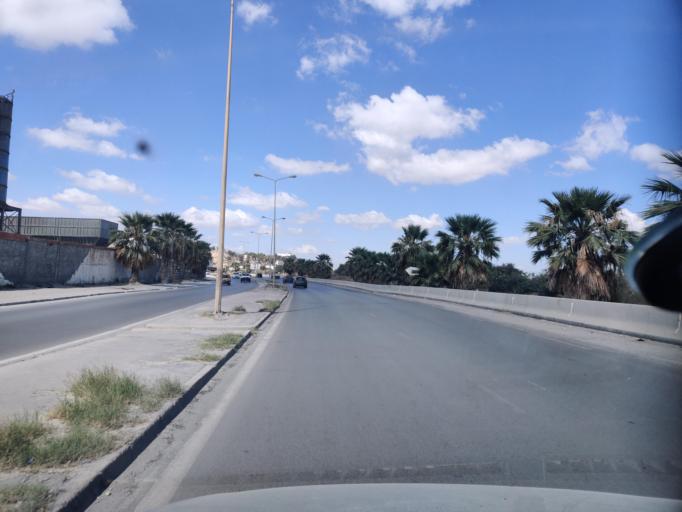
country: TN
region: Bin 'Arus
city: Ben Arous
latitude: 36.7805
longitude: 10.2025
